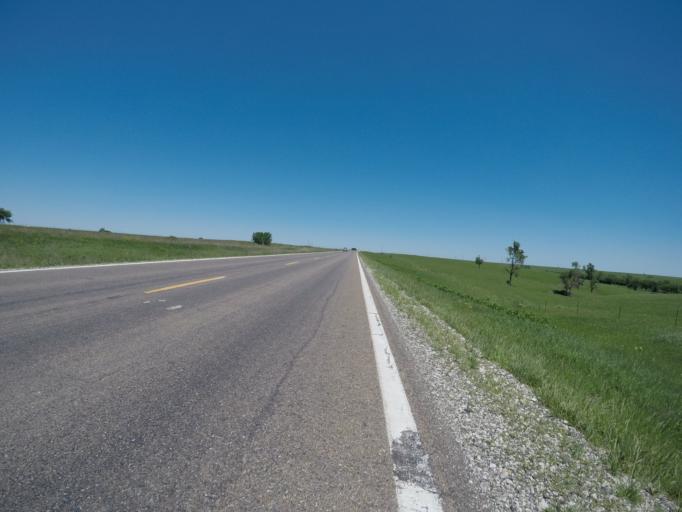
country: US
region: Kansas
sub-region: Morris County
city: Council Grove
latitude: 38.5599
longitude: -96.5220
